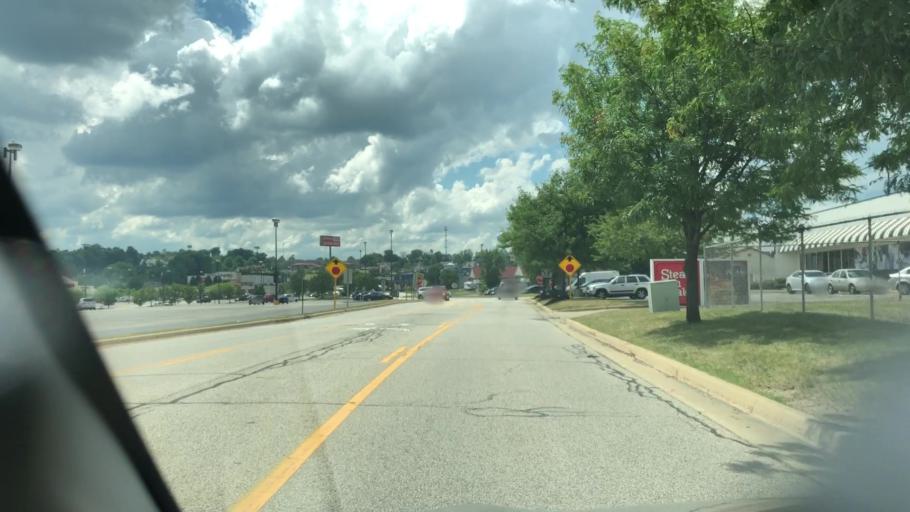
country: US
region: Ohio
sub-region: Summit County
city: Montrose-Ghent
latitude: 41.1334
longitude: -81.6425
